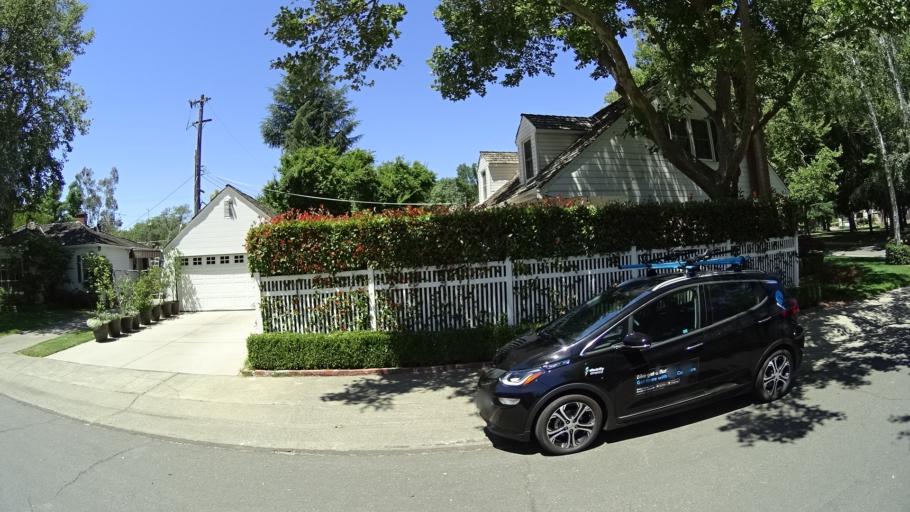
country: US
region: California
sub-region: Sacramento County
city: Sacramento
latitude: 38.5453
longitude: -121.5076
